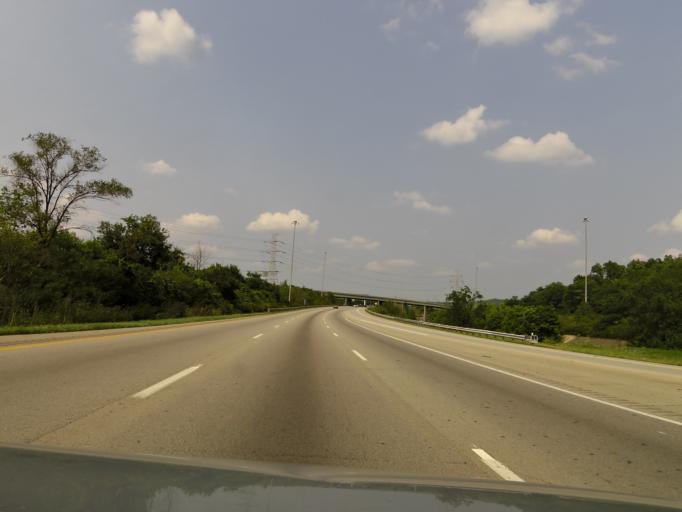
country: US
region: Ohio
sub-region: Hamilton County
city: Lockland
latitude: 39.2084
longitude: -84.4633
